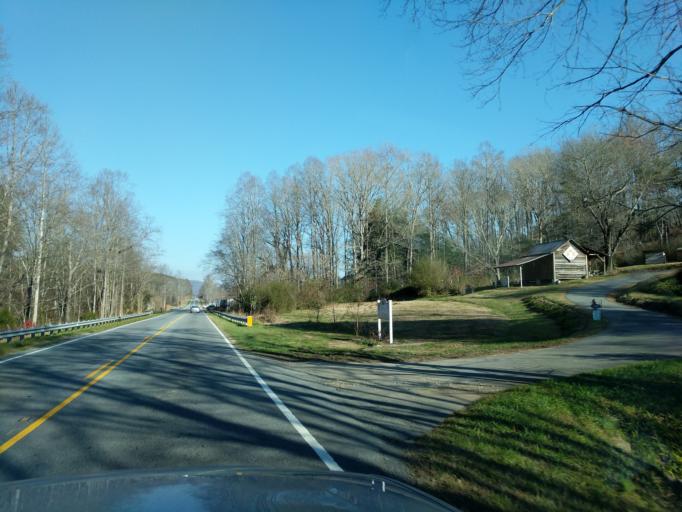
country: US
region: North Carolina
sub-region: McDowell County
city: West Marion
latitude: 35.5906
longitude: -81.9833
